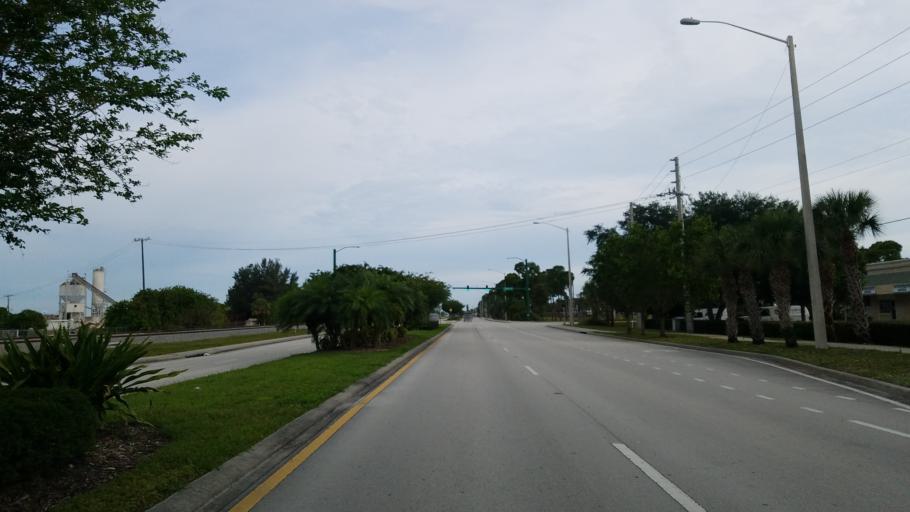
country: US
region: Florida
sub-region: Martin County
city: Stuart
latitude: 27.1751
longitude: -80.2300
